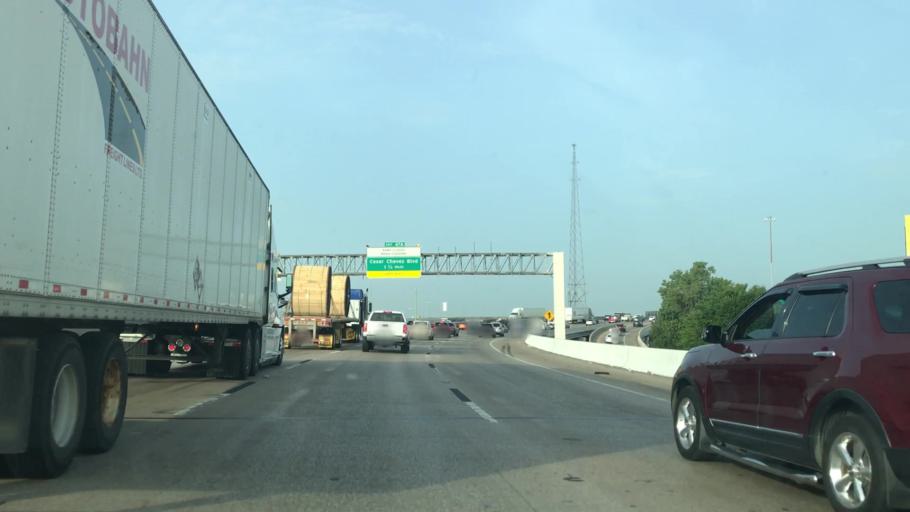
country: US
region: Texas
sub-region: Dallas County
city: Dallas
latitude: 32.7825
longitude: -96.7700
